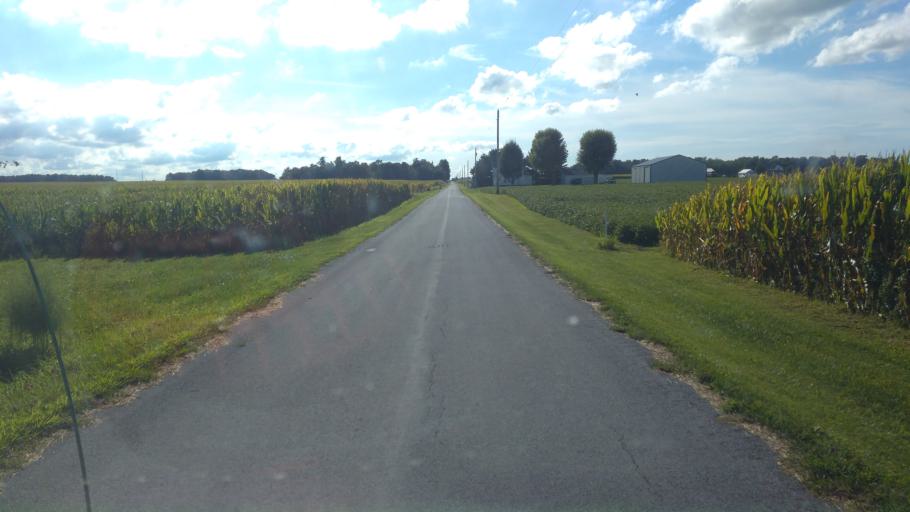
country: US
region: Ohio
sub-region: Hardin County
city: Kenton
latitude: 40.7177
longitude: -83.6673
